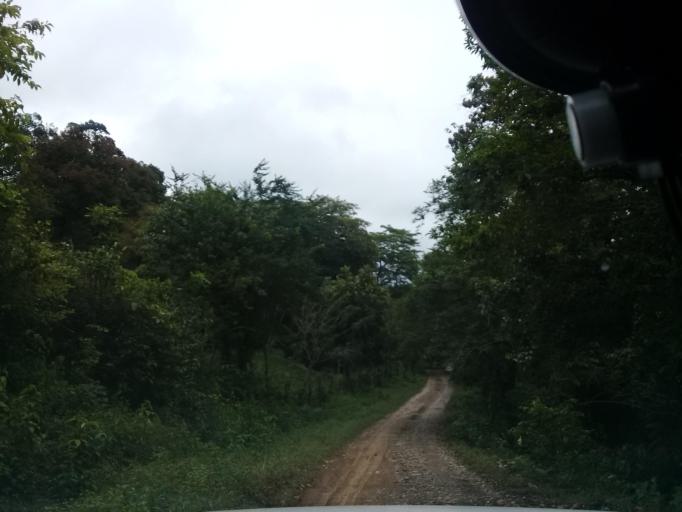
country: MX
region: Veracruz
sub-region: Chalma
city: San Pedro Coyutla
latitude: 21.2379
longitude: -98.4296
